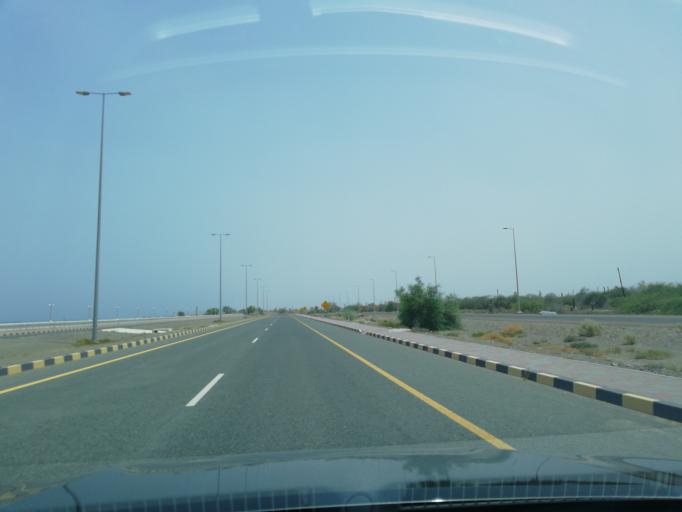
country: OM
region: Al Batinah
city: Al Liwa'
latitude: 24.6245
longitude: 56.5311
